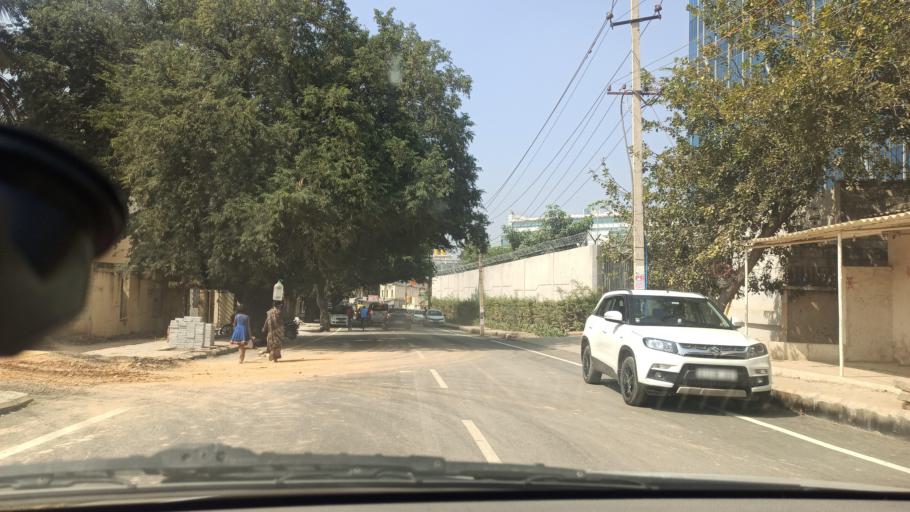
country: IN
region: Karnataka
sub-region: Bangalore Urban
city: Bangalore
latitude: 12.9400
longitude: 77.6931
